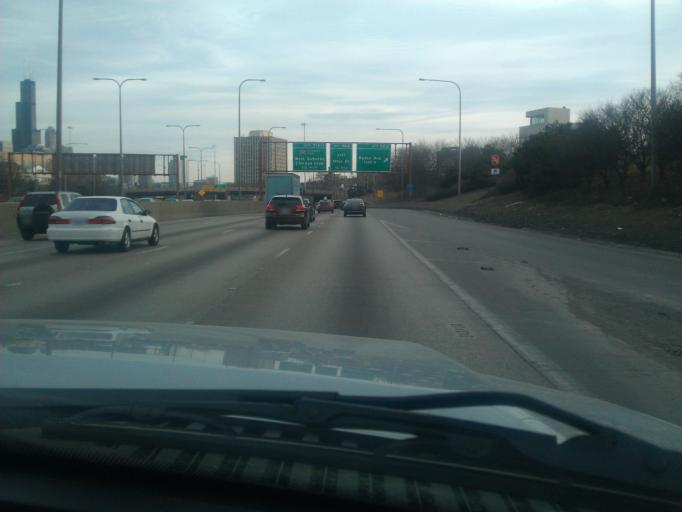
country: US
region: Illinois
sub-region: Cook County
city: Chicago
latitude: 41.8986
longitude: -87.6600
